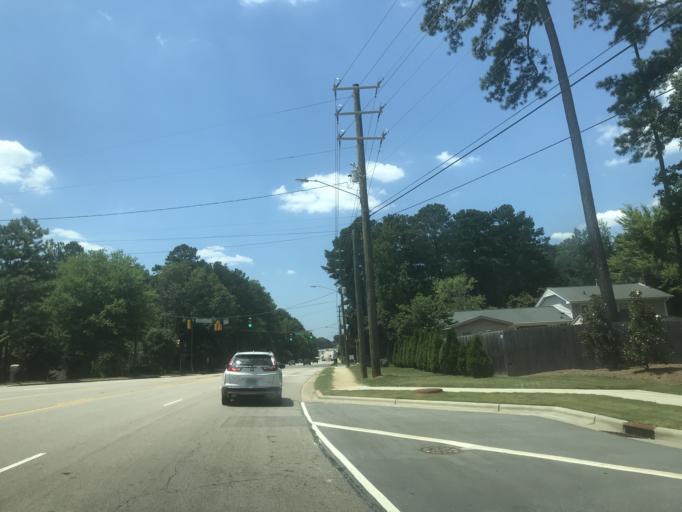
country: US
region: North Carolina
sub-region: Wake County
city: Cary
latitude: 35.7665
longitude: -78.7566
